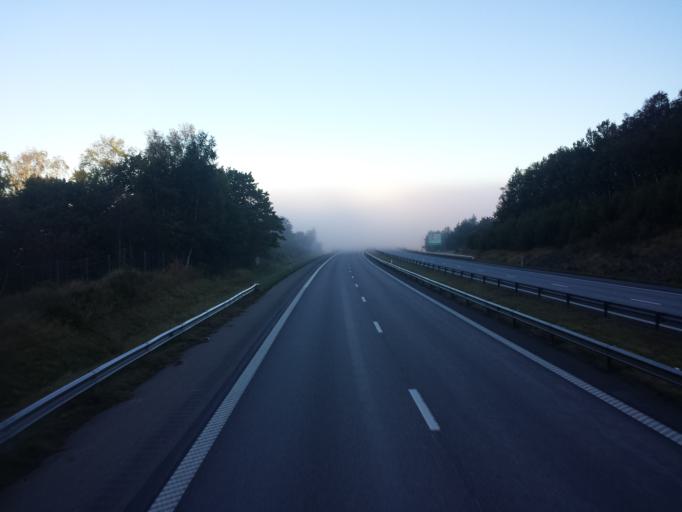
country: SE
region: Halland
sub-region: Kungsbacka Kommun
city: Kungsbacka
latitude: 57.4504
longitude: 12.0970
